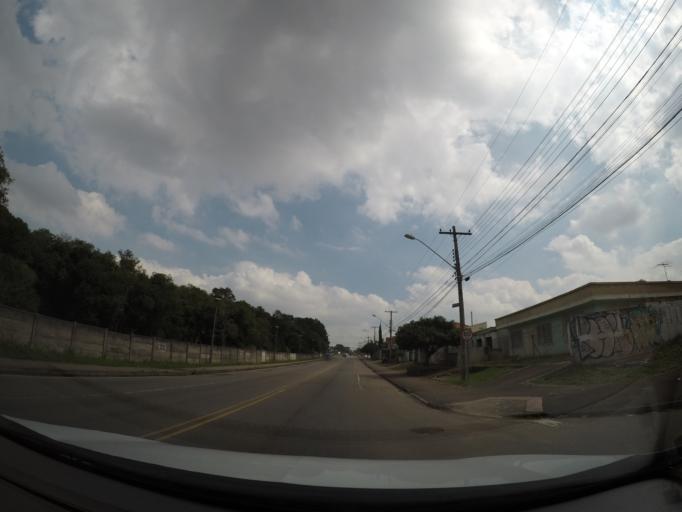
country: BR
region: Parana
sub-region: Sao Jose Dos Pinhais
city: Sao Jose dos Pinhais
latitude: -25.5063
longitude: -49.2449
